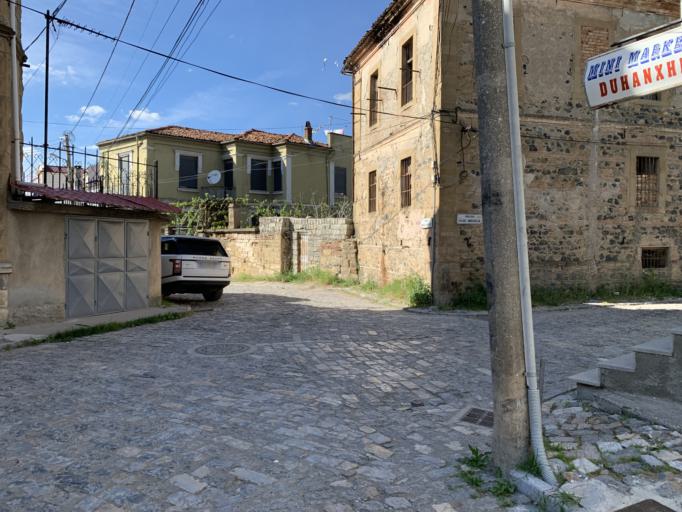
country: AL
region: Korce
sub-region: Rrethi i Korces
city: Korce
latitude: 40.6138
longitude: 20.7828
